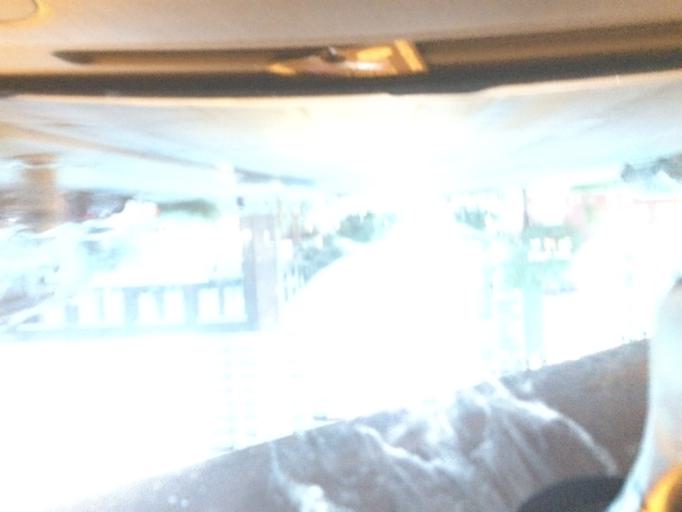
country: CA
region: Quebec
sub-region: Montreal
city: Montreal
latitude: 45.4948
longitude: -73.5564
